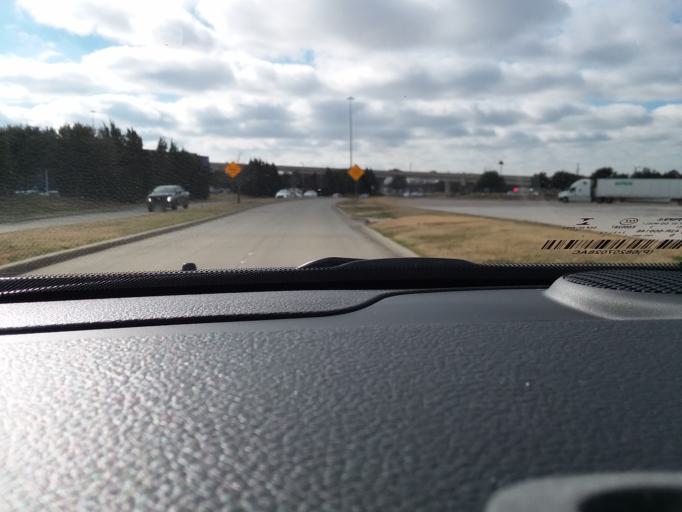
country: US
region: Texas
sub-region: Collin County
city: Frisco
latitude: 33.0960
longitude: -96.8204
